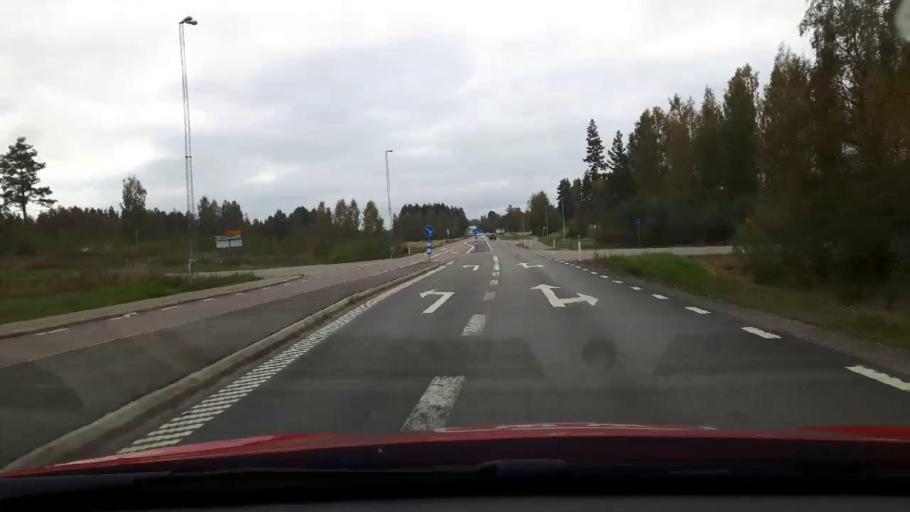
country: SE
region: Gaevleborg
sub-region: Bollnas Kommun
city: Bollnas
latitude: 61.3770
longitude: 16.3878
